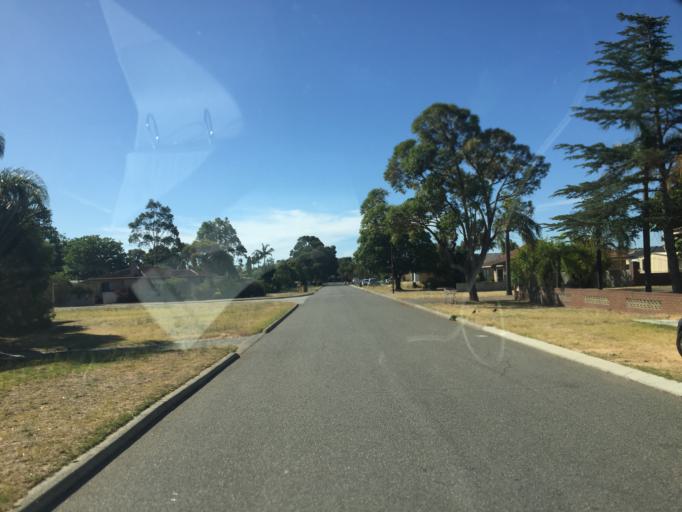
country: AU
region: Western Australia
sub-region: Gosnells
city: Gosnells
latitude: -32.0593
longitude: 116.0032
